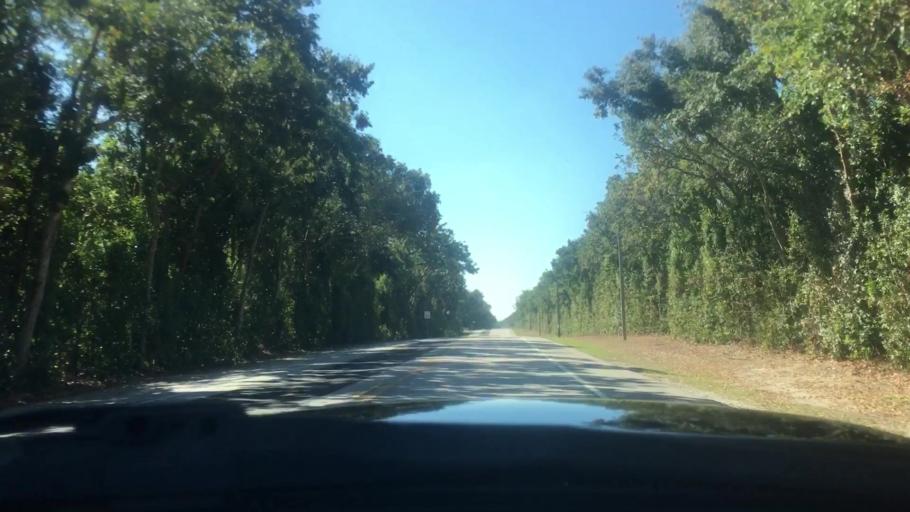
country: US
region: Florida
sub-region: Monroe County
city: North Key Largo
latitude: 25.2412
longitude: -80.3217
